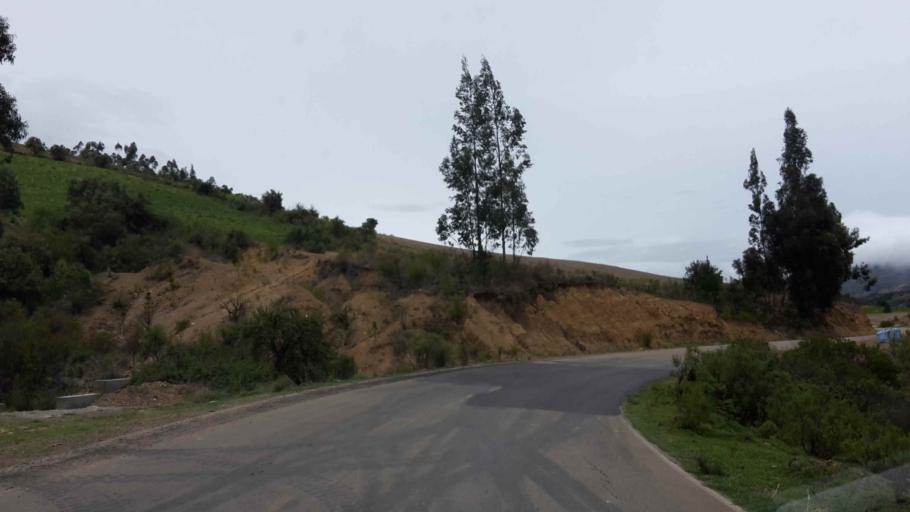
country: BO
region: Cochabamba
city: Totora
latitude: -17.7002
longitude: -65.2148
